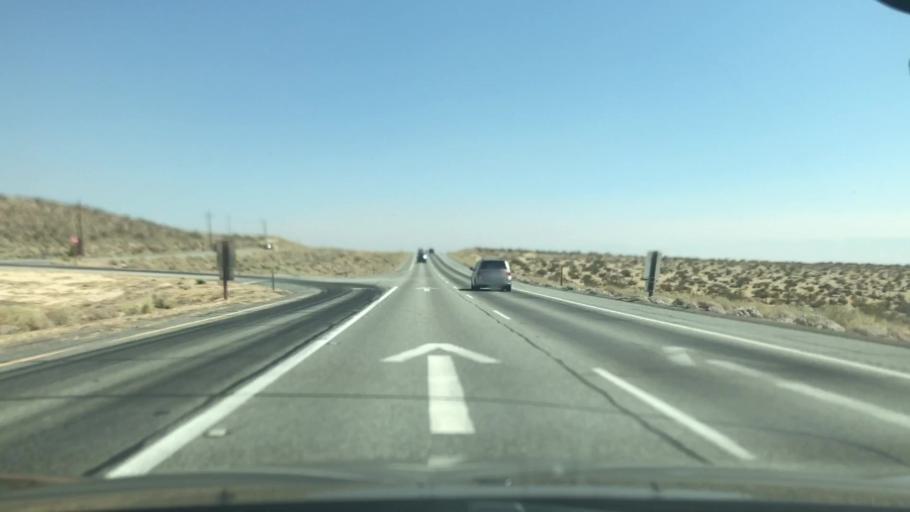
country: US
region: California
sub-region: Kern County
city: Inyokern
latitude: 35.6677
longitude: -117.8716
